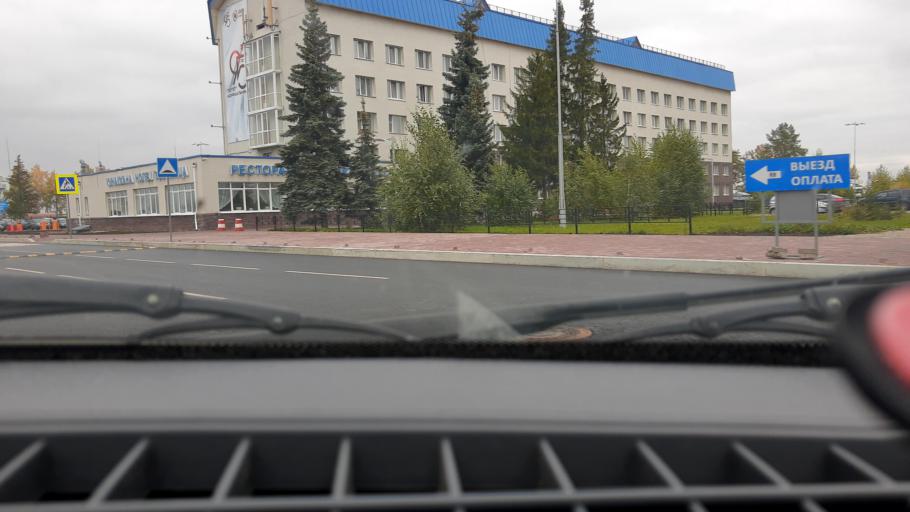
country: RU
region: Bashkortostan
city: Ufa
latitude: 54.5658
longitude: 55.8859
